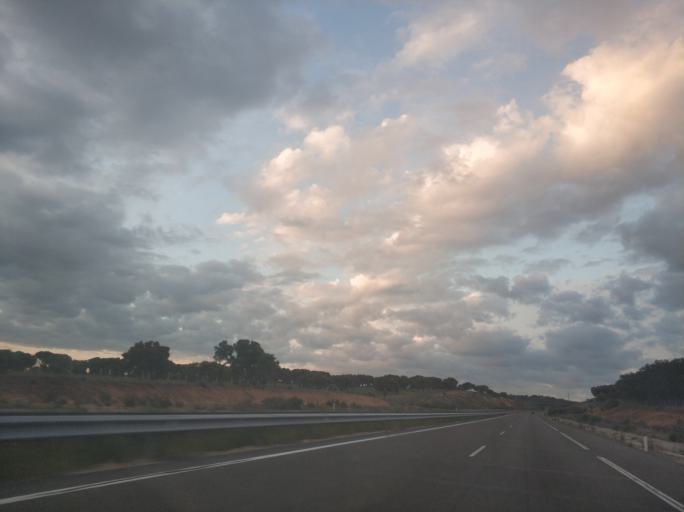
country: ES
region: Castille and Leon
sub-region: Provincia de Salamanca
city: Mozarbez
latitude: 40.8267
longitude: -5.6355
